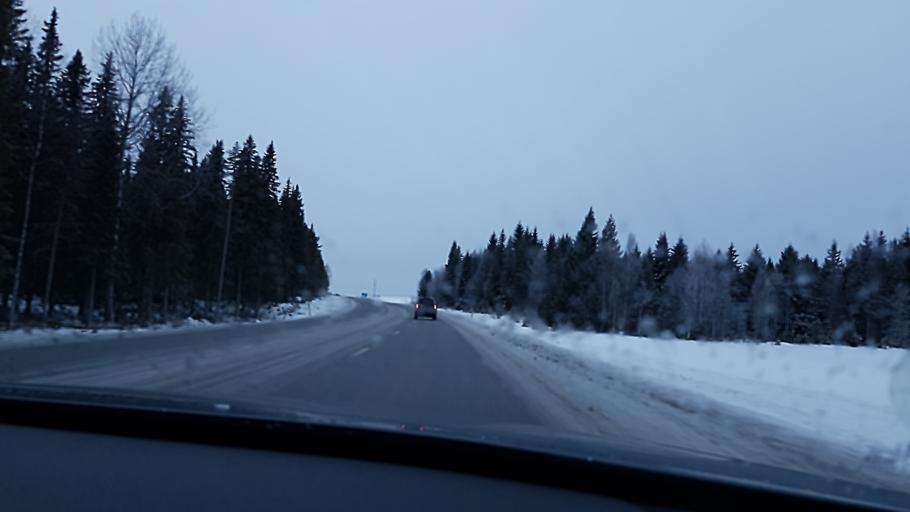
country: SE
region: Jaemtland
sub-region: OEstersunds Kommun
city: Lit
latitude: 63.2439
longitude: 14.7840
